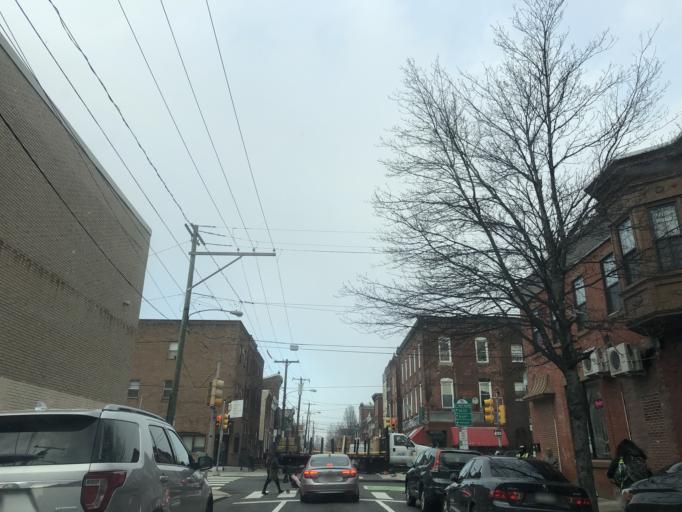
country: US
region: Pennsylvania
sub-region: Philadelphia County
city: Philadelphia
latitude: 39.9238
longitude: -75.1677
